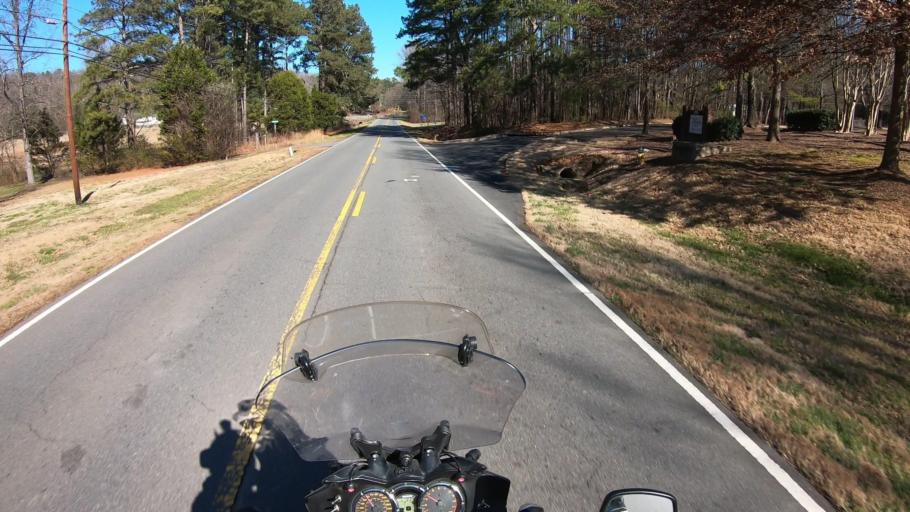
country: US
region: Georgia
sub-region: Bartow County
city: Cartersville
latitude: 34.2587
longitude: -84.8083
